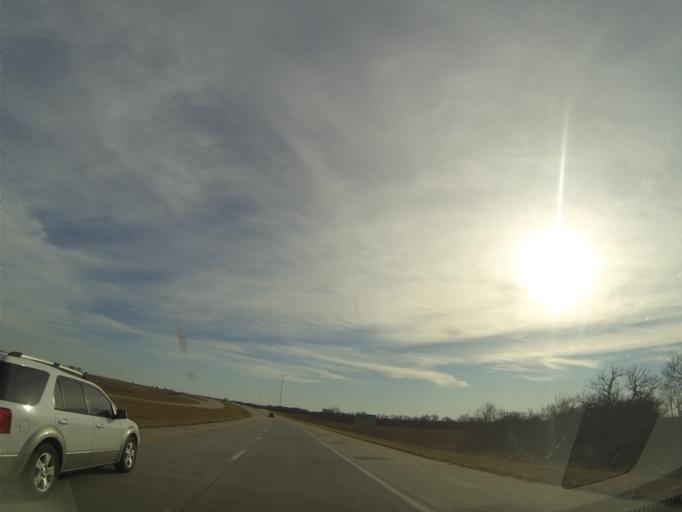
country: US
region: Kansas
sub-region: Ottawa County
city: Minneapolis
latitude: 39.1240
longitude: -97.6694
